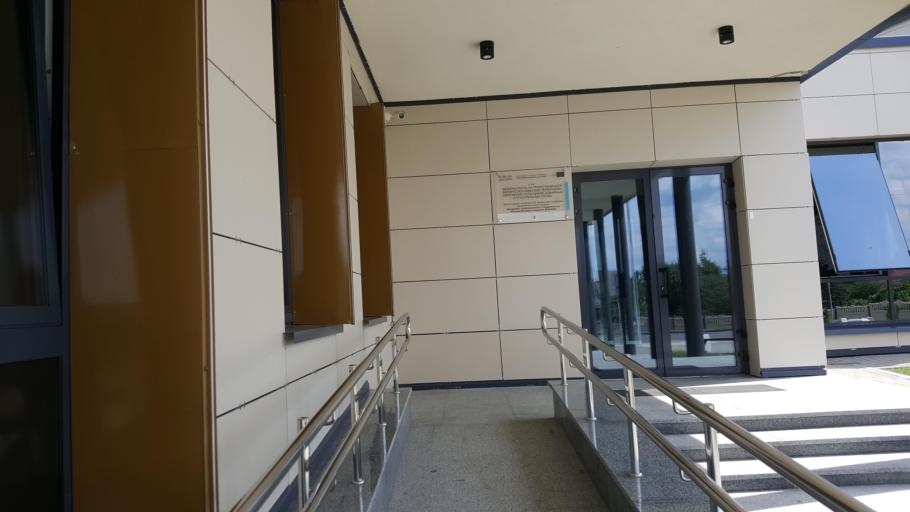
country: BY
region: Brest
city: Kamyanyets
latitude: 52.3981
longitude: 23.8239
